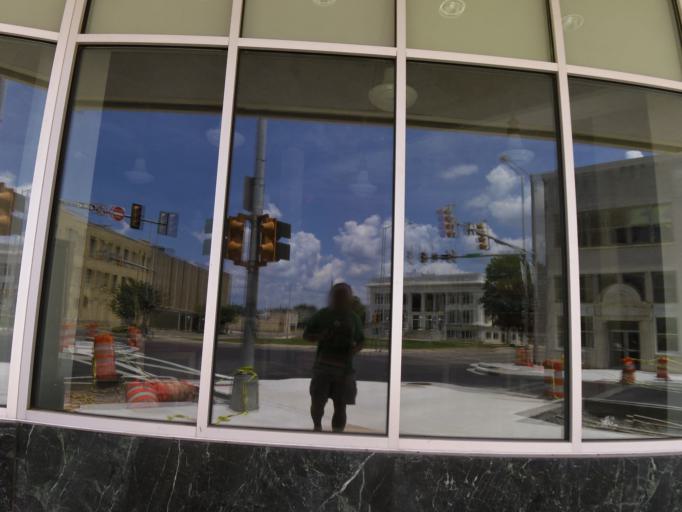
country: US
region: Mississippi
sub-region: Lauderdale County
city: Meridian
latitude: 32.3638
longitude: -88.7012
